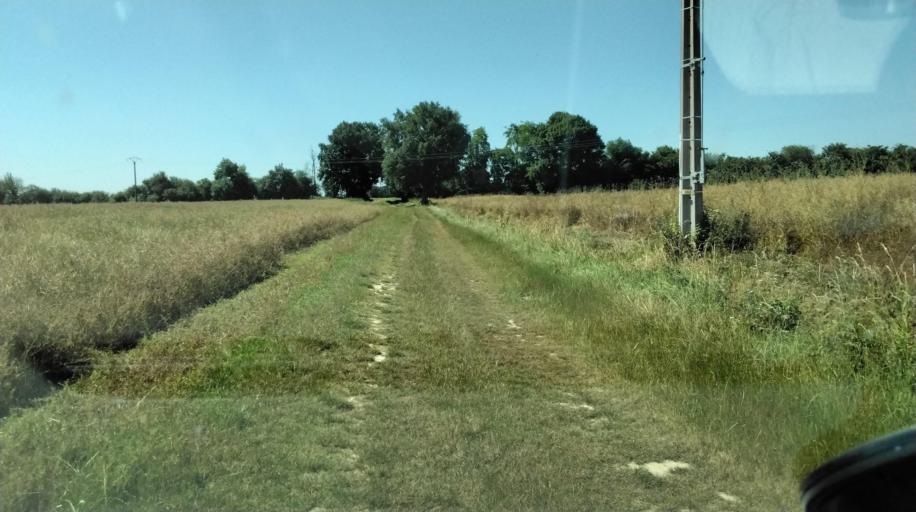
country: FR
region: Midi-Pyrenees
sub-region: Departement de la Haute-Garonne
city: Sainte-Foy-de-Peyrolieres
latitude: 43.4909
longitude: 1.1563
